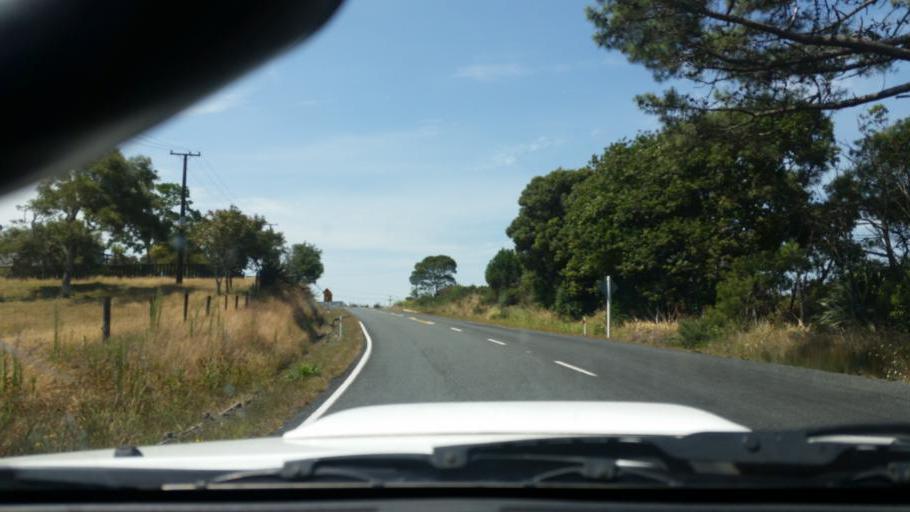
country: NZ
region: Northland
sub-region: Kaipara District
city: Dargaville
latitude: -36.0339
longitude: 173.9210
